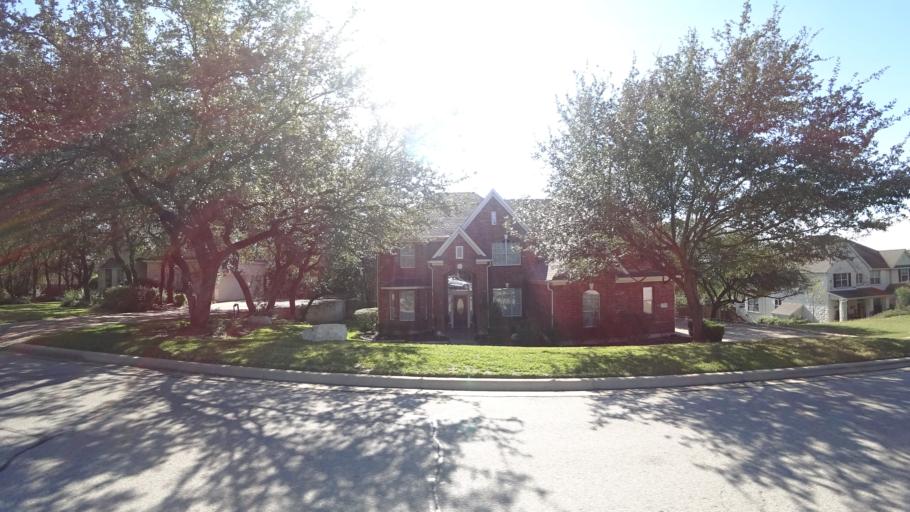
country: US
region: Texas
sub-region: Travis County
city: Hudson Bend
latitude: 30.3759
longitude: -97.9028
